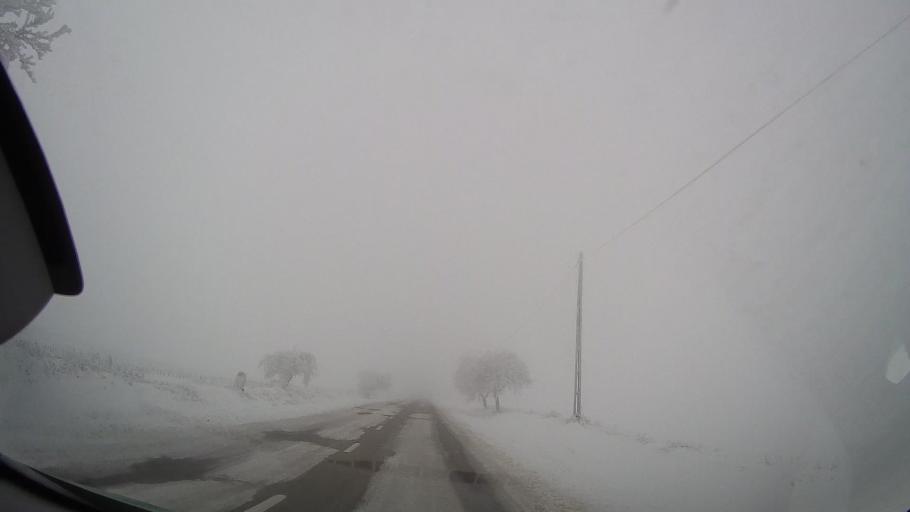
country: RO
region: Neamt
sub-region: Comuna Valea Ursului
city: Valea Ursului
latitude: 46.8063
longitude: 27.0701
